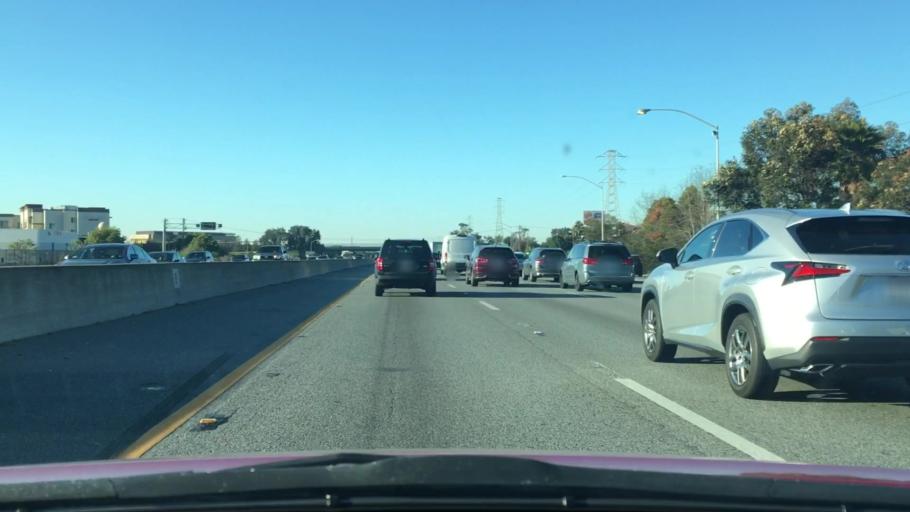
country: US
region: California
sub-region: San Mateo County
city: San Carlos
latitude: 37.5112
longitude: -122.2523
